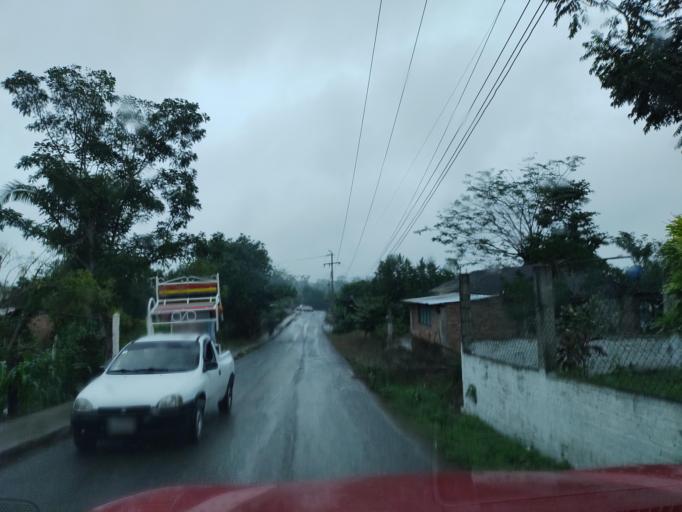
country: MX
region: Veracruz
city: Agua Dulce
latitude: 20.3331
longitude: -97.3252
